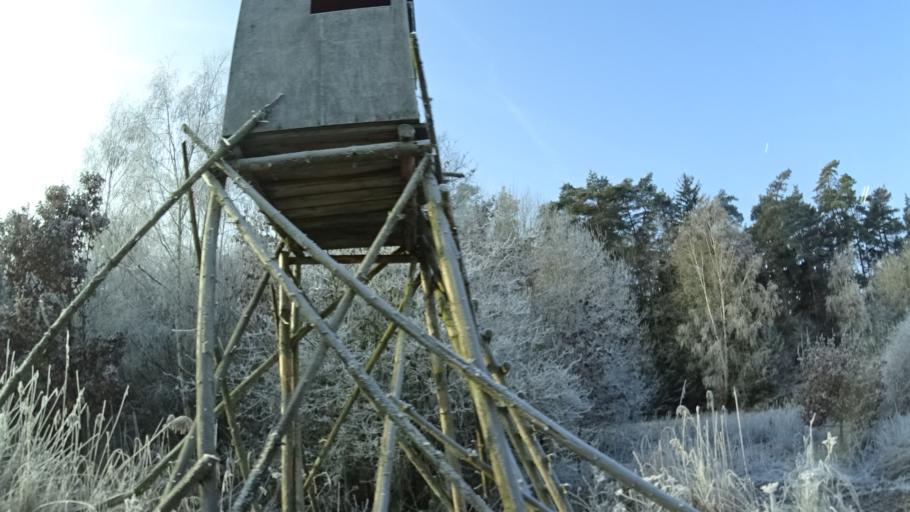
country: DE
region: Bavaria
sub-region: Upper Franconia
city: Sesslach
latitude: 50.2088
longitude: 10.8098
